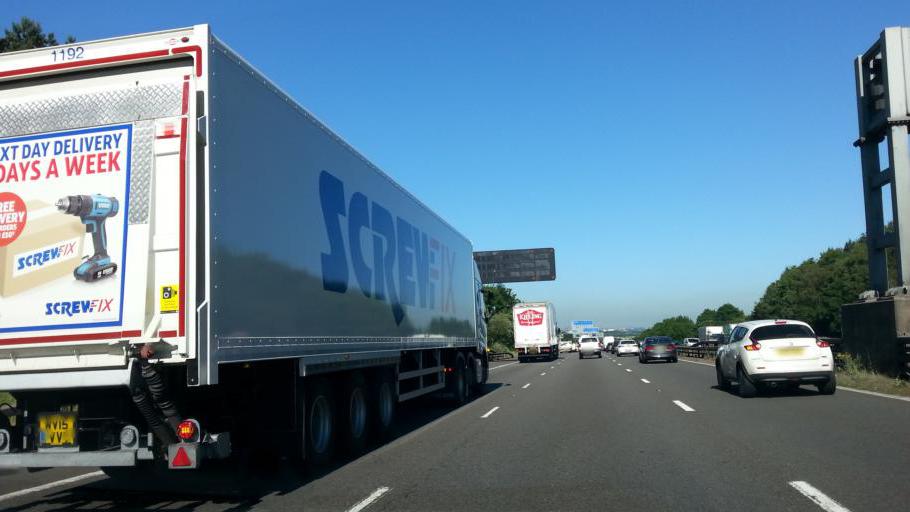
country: GB
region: England
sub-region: Solihull
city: Meriden
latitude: 52.4689
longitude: -1.6400
